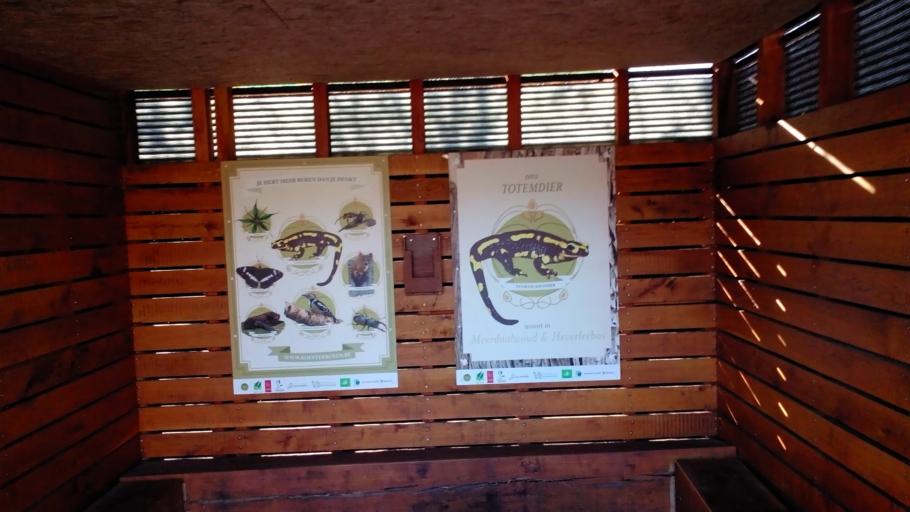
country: BE
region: Flanders
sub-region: Provincie Vlaams-Brabant
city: Oud-Heverlee
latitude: 50.8057
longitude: 4.6634
